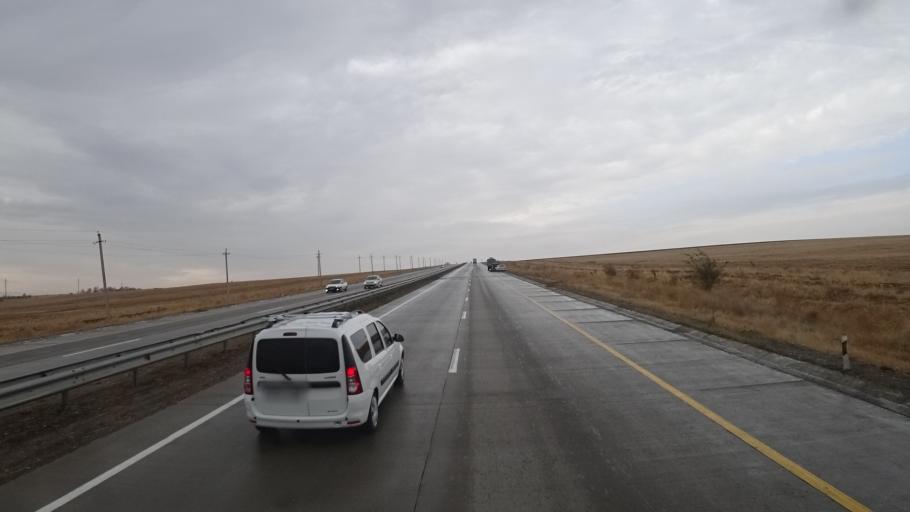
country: KZ
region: Ongtustik Qazaqstan
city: Sastobe
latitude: 42.5245
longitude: 70.0096
